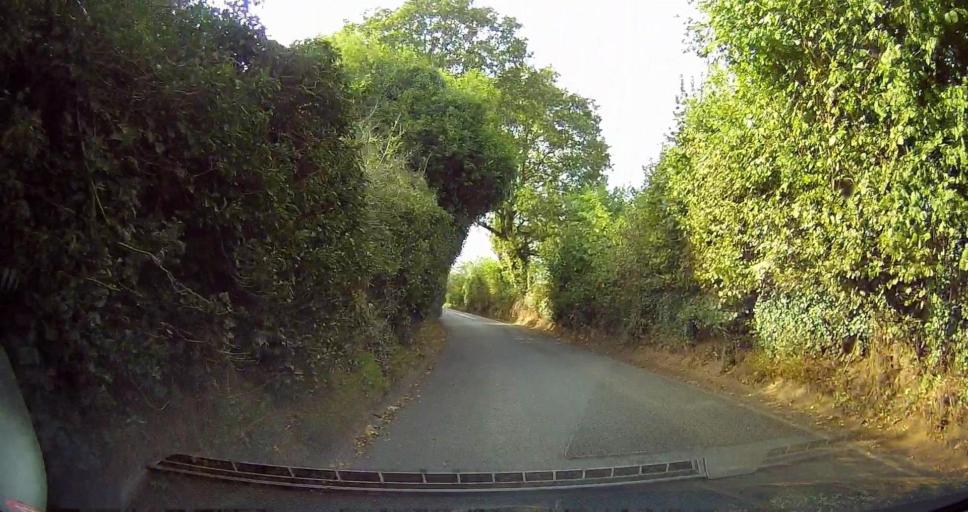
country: GB
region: England
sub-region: Kent
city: Longfield
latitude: 51.4192
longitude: 0.3002
